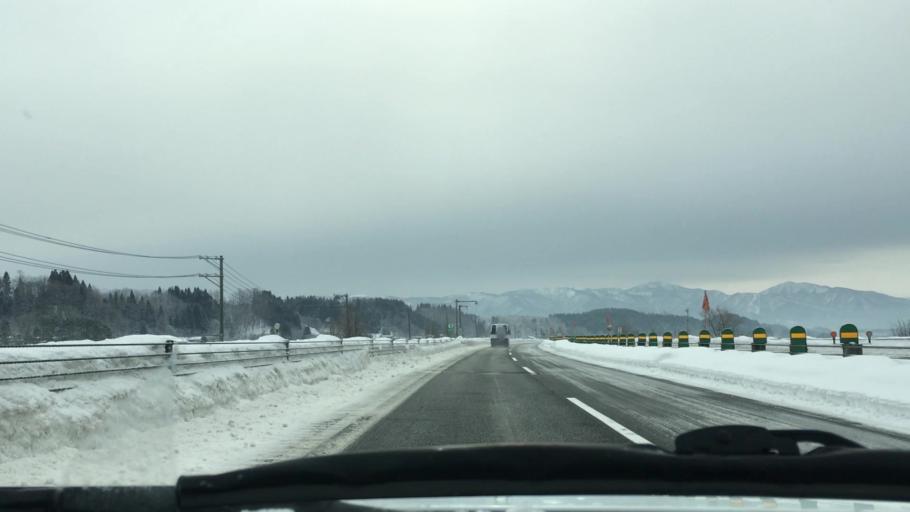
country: JP
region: Akita
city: Hanawa
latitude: 40.2968
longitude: 140.7530
